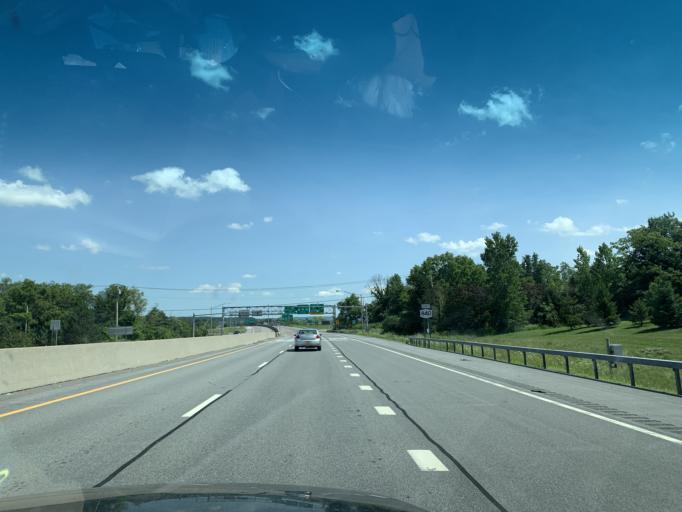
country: US
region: New York
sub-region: Oneida County
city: New Hartford
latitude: 43.0831
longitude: -75.2958
